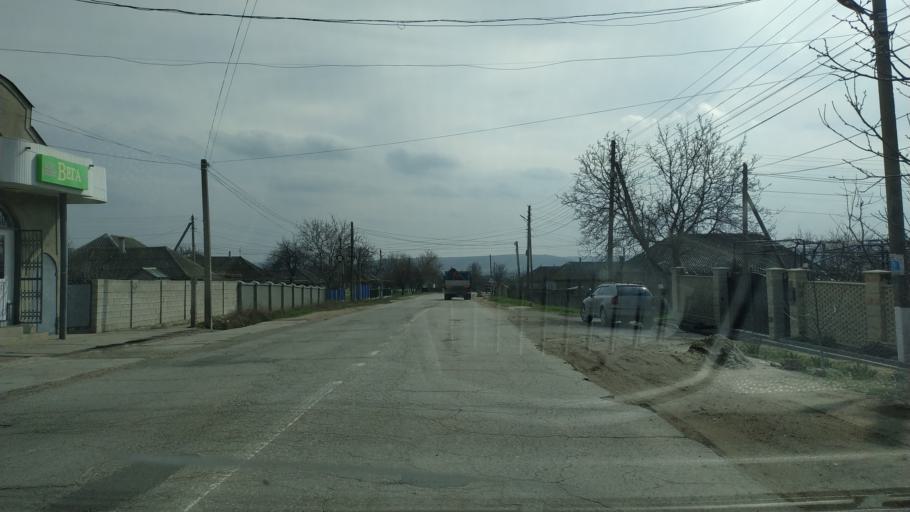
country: MD
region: Gagauzia
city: Vulcanesti
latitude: 45.6943
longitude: 28.4045
